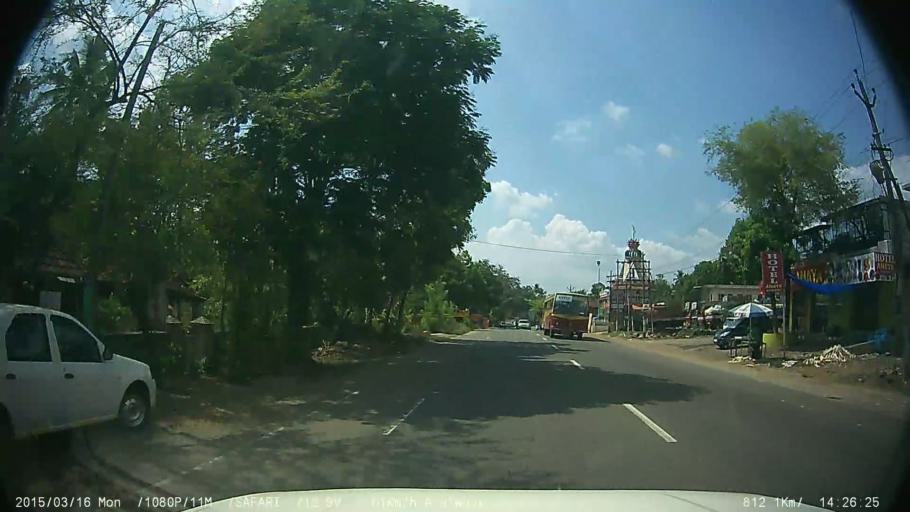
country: IN
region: Kerala
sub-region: Ernakulam
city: Perumbavoor
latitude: 10.0916
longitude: 76.4963
